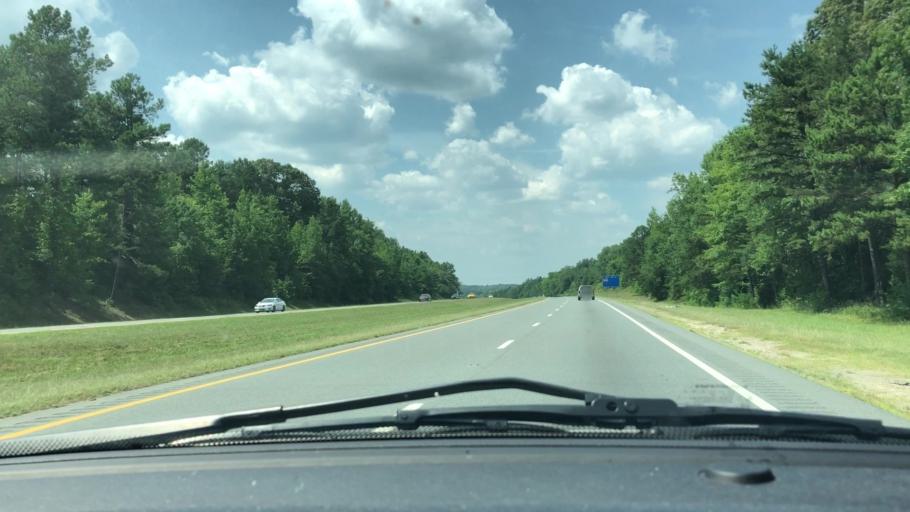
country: US
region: North Carolina
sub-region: Guilford County
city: Forest Oaks
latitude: 35.9491
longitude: -79.6900
